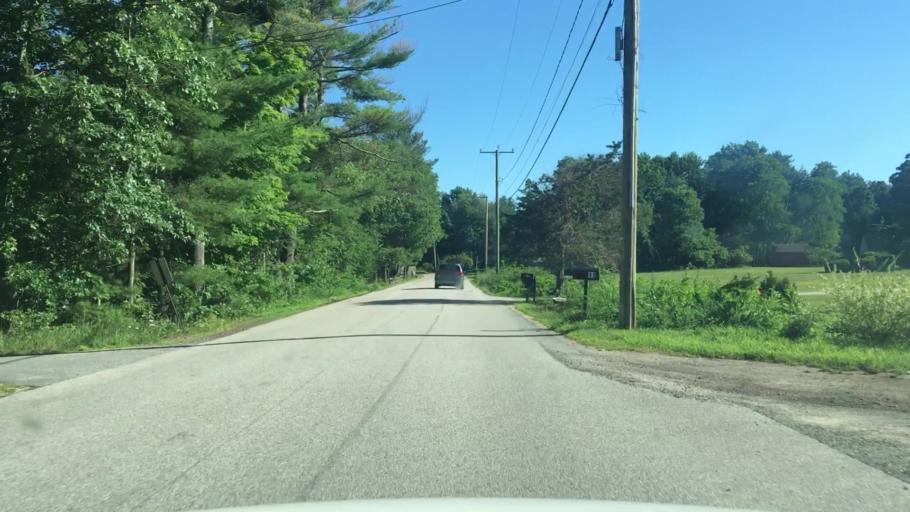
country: US
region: New Hampshire
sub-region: Rockingham County
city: Brentwood
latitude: 42.9940
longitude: -71.0147
